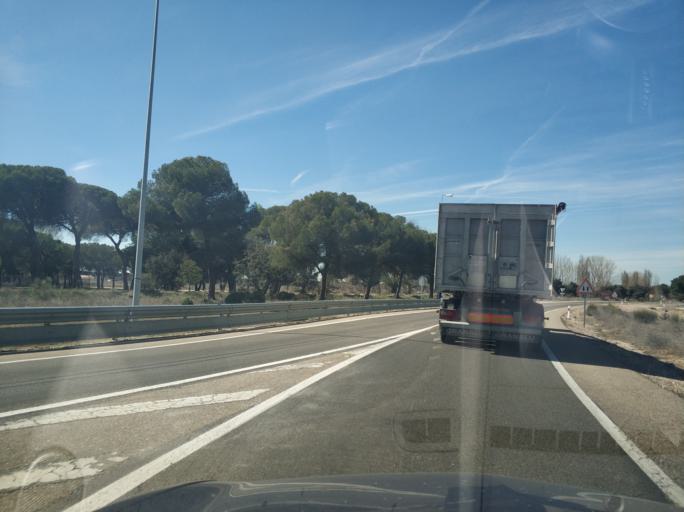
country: ES
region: Castille and Leon
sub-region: Provincia de Valladolid
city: Viana de Cega
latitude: 41.5622
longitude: -4.7875
